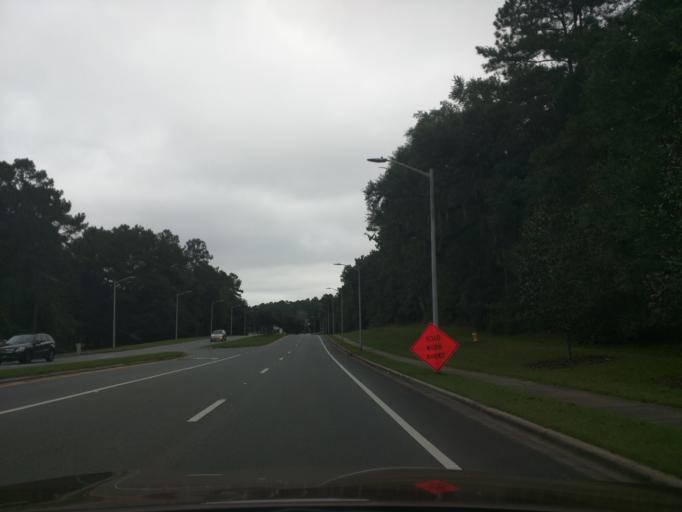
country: US
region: Florida
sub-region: Leon County
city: Tallahassee
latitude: 30.4315
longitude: -84.2020
